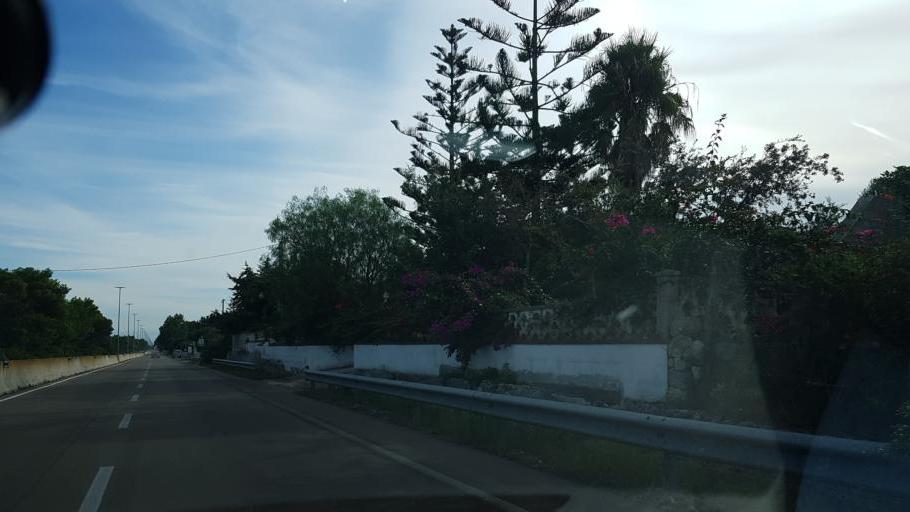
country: IT
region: Apulia
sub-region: Provincia di Lecce
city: Struda
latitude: 40.3839
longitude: 18.2828
